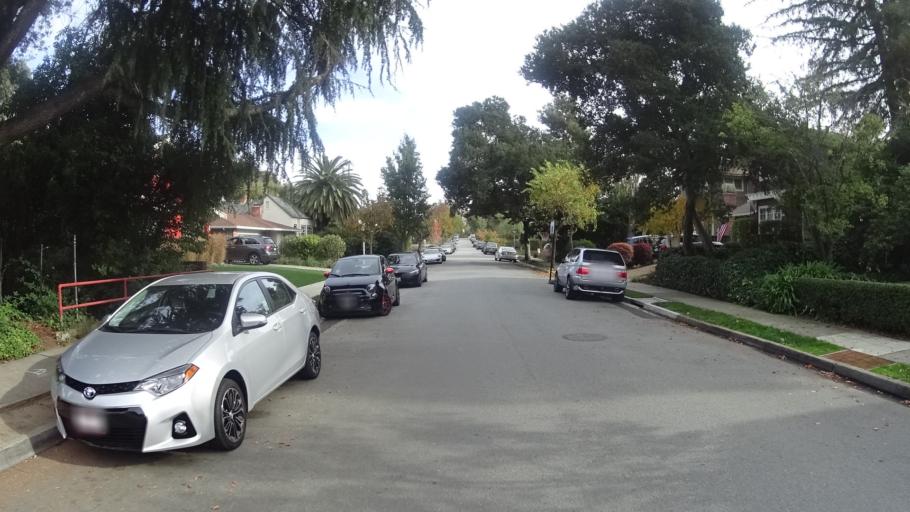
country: US
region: California
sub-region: San Mateo County
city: Burlingame
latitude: 37.5849
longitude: -122.3693
